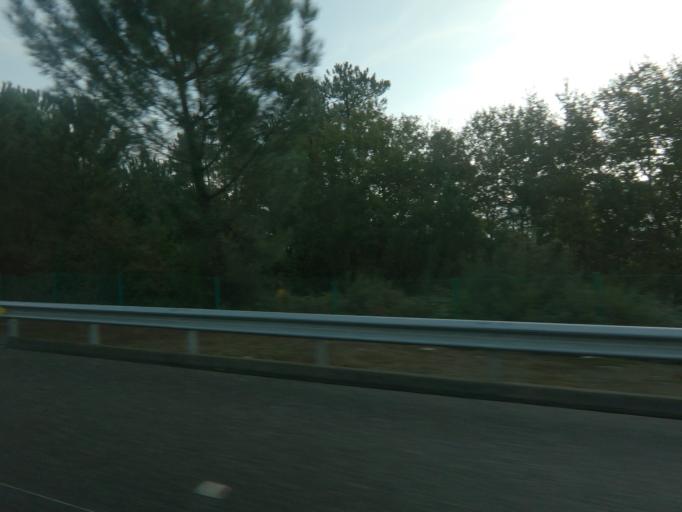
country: ES
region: Galicia
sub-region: Provincia de Pontevedra
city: Tui
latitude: 42.0971
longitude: -8.6438
